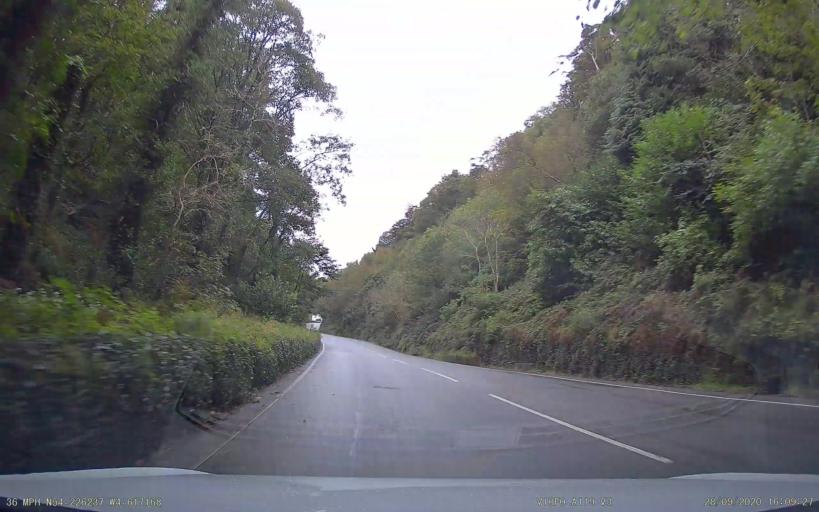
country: IM
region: Douglas
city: Douglas
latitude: 54.2262
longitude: -4.6172
